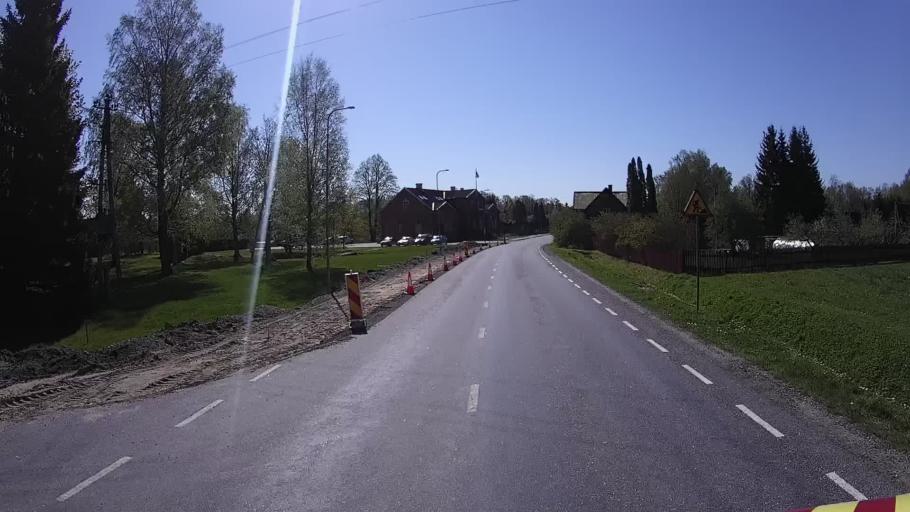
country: EE
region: Paernumaa
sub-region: Tootsi vald
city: Tootsi
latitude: 58.4866
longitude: 24.8132
